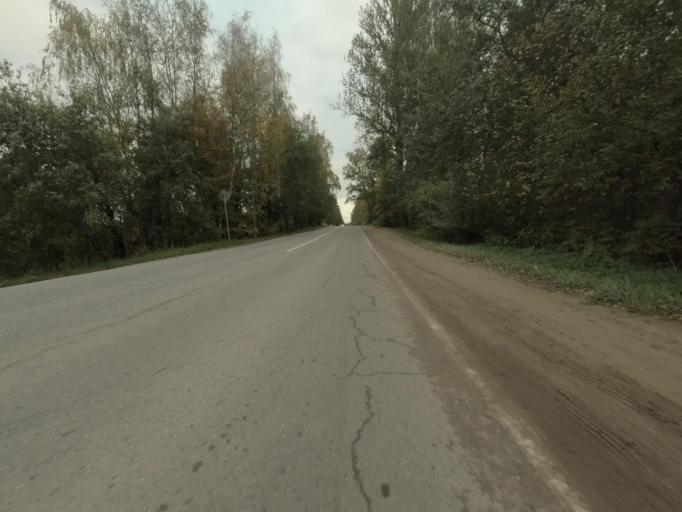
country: RU
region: Leningrad
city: Pavlovo
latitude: 59.7795
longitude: 30.9720
